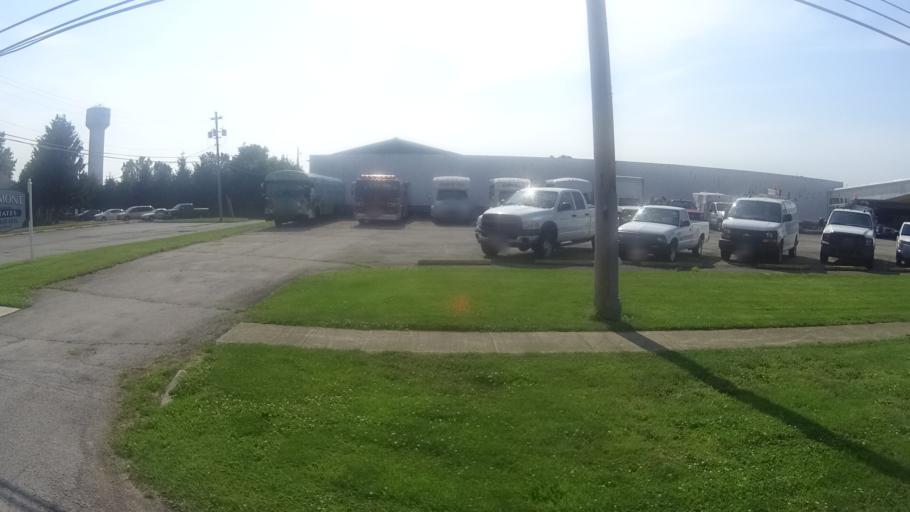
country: US
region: Ohio
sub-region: Huron County
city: Bellevue
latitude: 41.2858
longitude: -82.8372
